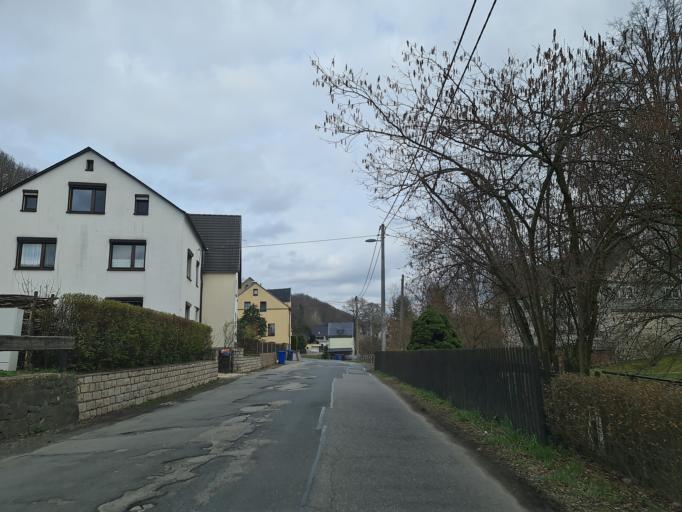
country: DE
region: Saxony
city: Reinsdorf
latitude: 50.7119
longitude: 12.6123
